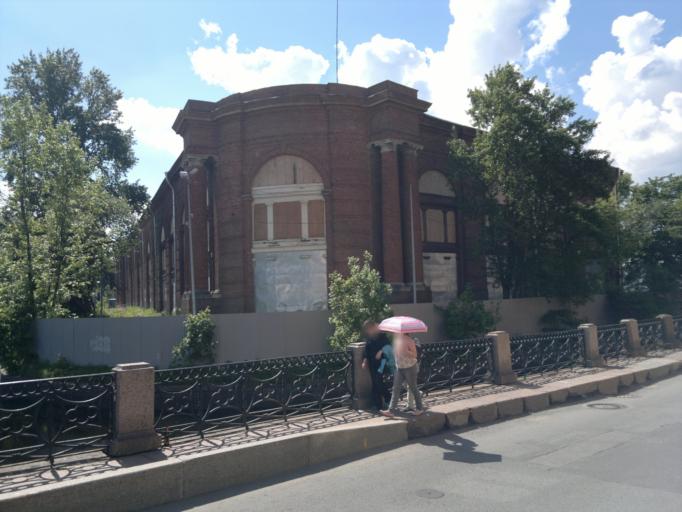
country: RU
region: St.-Petersburg
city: Saint Petersburg
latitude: 59.9315
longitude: 30.2918
